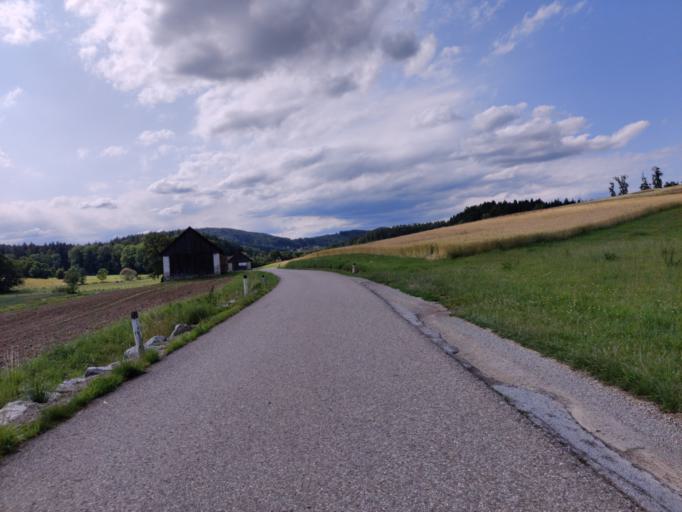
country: AT
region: Styria
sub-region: Politischer Bezirk Graz-Umgebung
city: Thal
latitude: 47.0592
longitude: 15.3518
